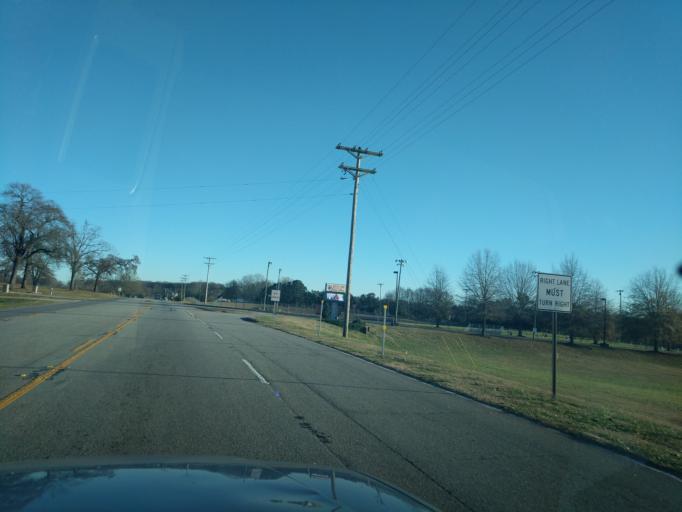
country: US
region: South Carolina
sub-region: Oconee County
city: Westminster
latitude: 34.6225
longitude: -83.0519
